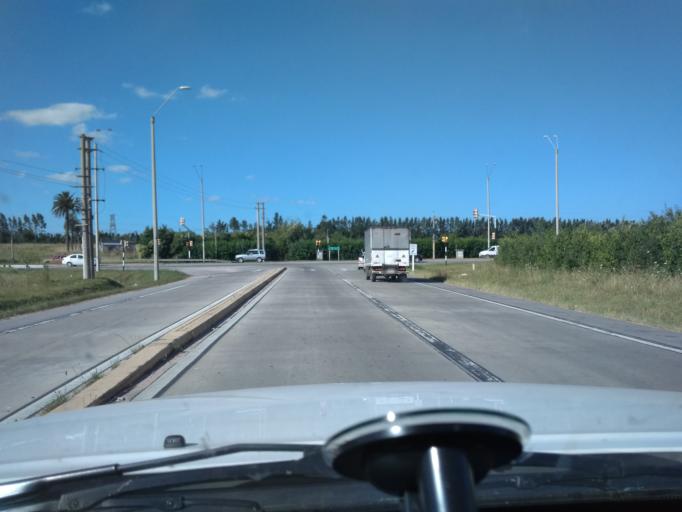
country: UY
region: Canelones
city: La Paz
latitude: -34.7918
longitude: -56.2113
